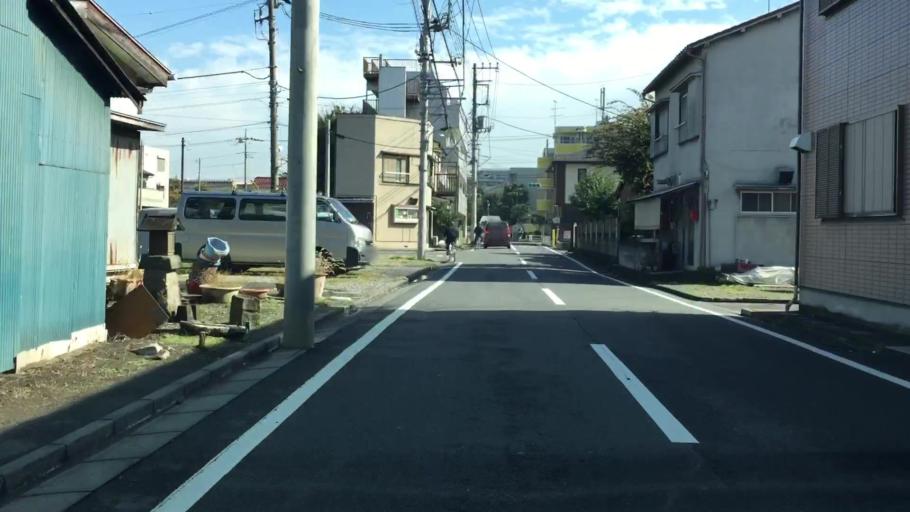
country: JP
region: Saitama
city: Soka
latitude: 35.7554
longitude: 139.8223
